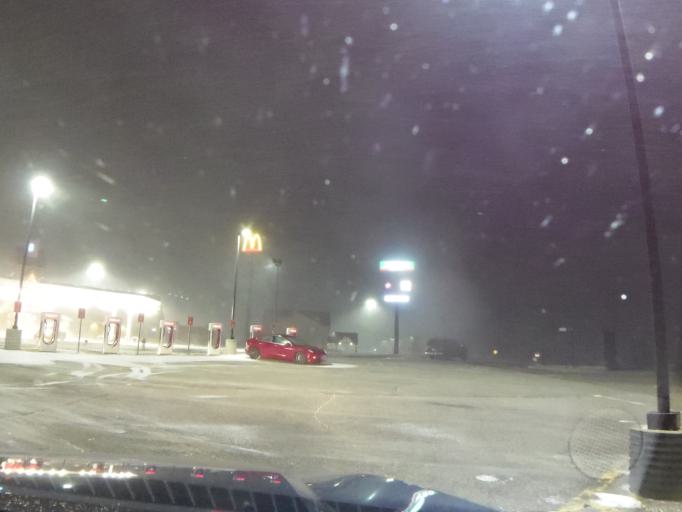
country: US
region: Minnesota
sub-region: Freeborn County
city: Albert Lea
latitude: 43.6577
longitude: -93.3184
